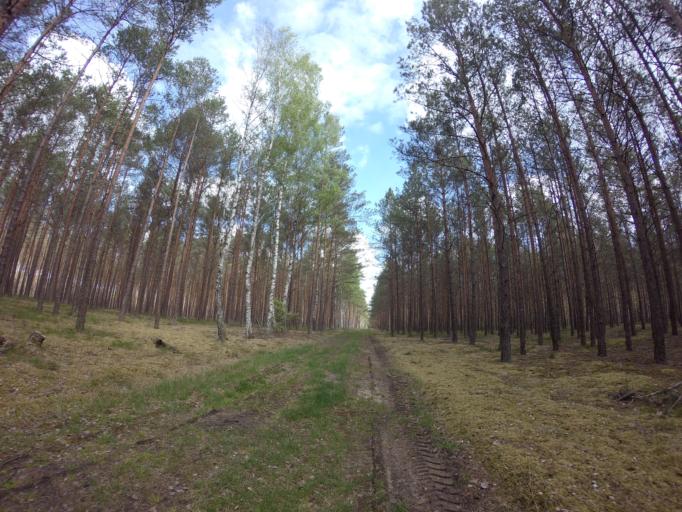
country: PL
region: West Pomeranian Voivodeship
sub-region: Powiat drawski
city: Kalisz Pomorski
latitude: 53.2001
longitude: 15.9838
